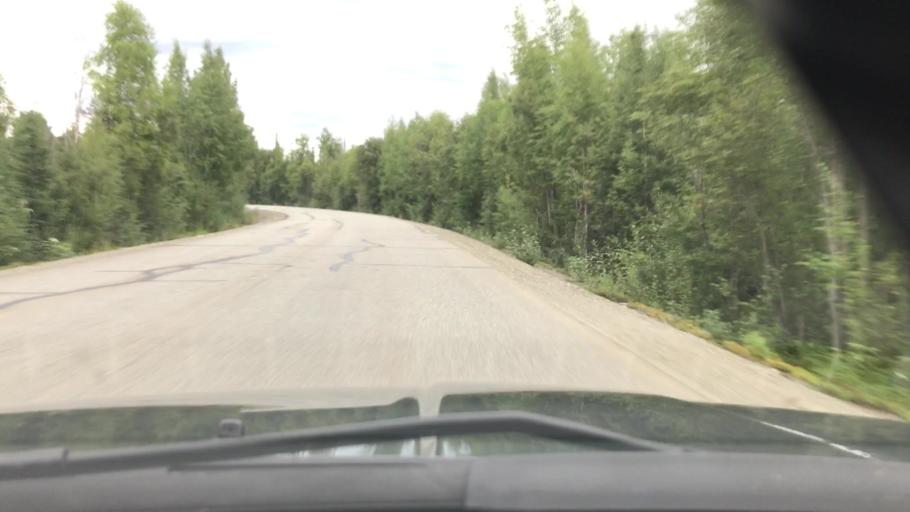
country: US
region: Alaska
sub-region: Matanuska-Susitna Borough
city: Willow
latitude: 61.7598
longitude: -150.1198
